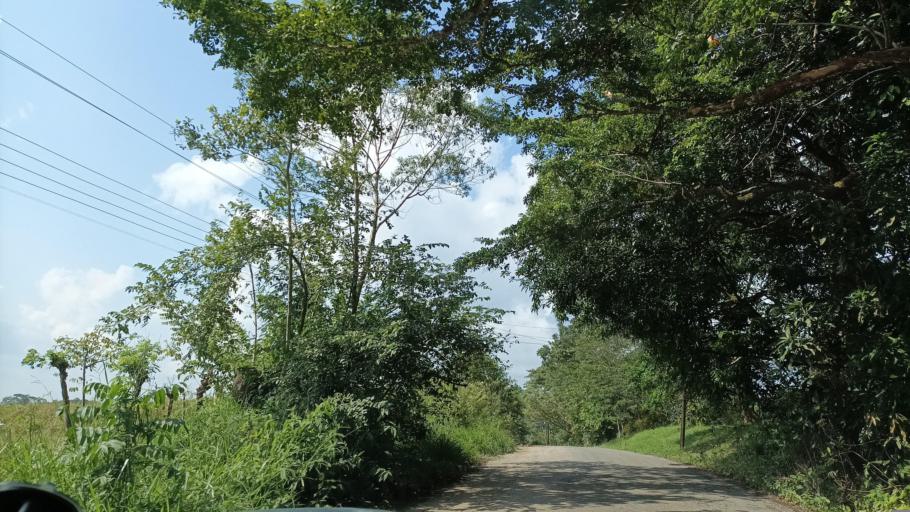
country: MX
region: Veracruz
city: Las Choapas
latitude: 17.7509
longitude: -94.1114
